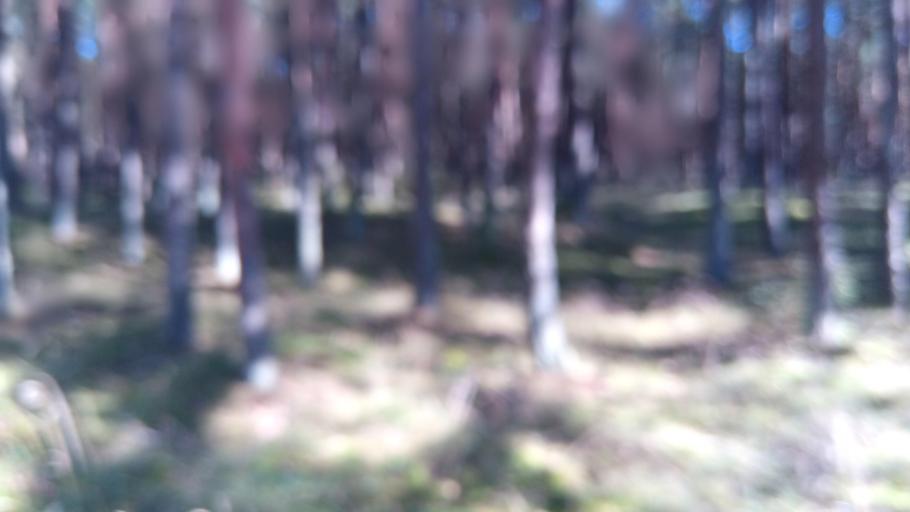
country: LT
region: Klaipedos apskritis
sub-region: Klaipeda
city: Klaipeda
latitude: 55.7056
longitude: 21.1004
